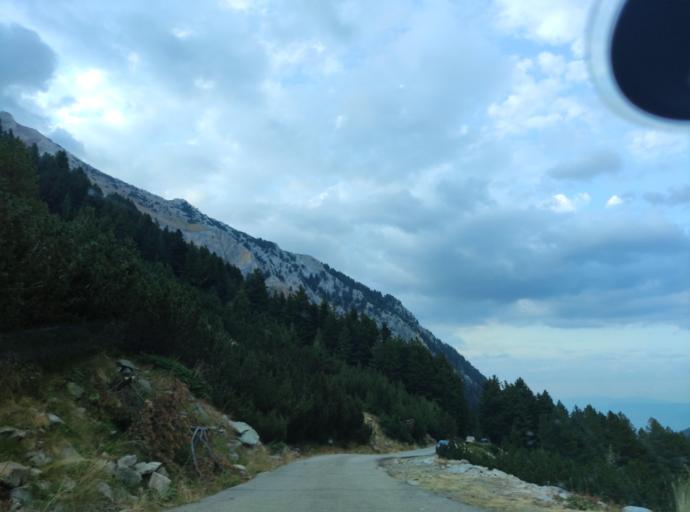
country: BG
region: Blagoevgrad
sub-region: Obshtina Bansko
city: Bansko
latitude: 41.7600
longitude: 23.4164
